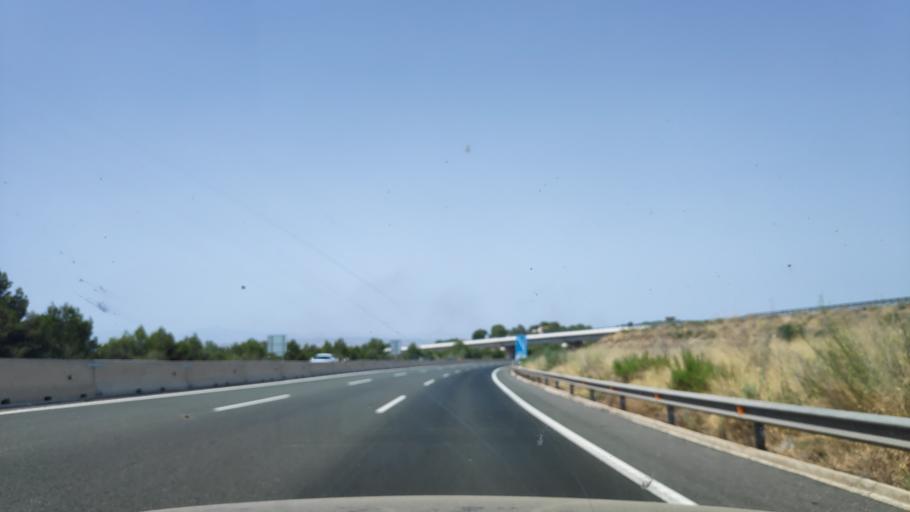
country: ES
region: Murcia
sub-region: Murcia
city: Alcantarilla
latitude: 37.9163
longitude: -1.1645
